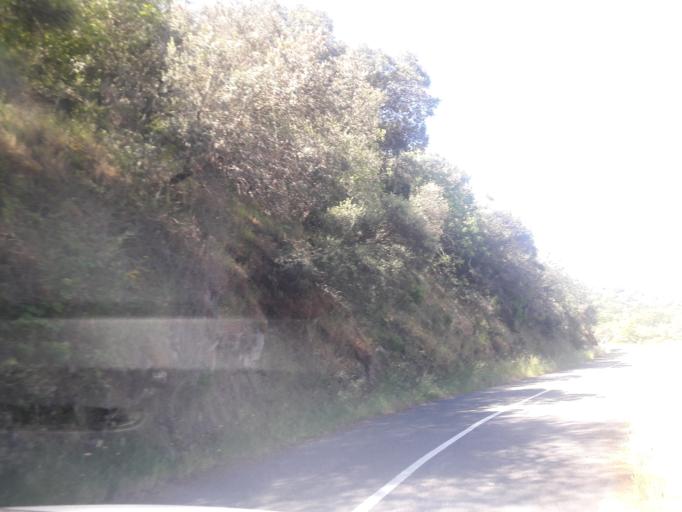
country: ES
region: Castille and Leon
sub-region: Provincia de Salamanca
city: Saucelle
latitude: 41.0244
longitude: -6.7413
